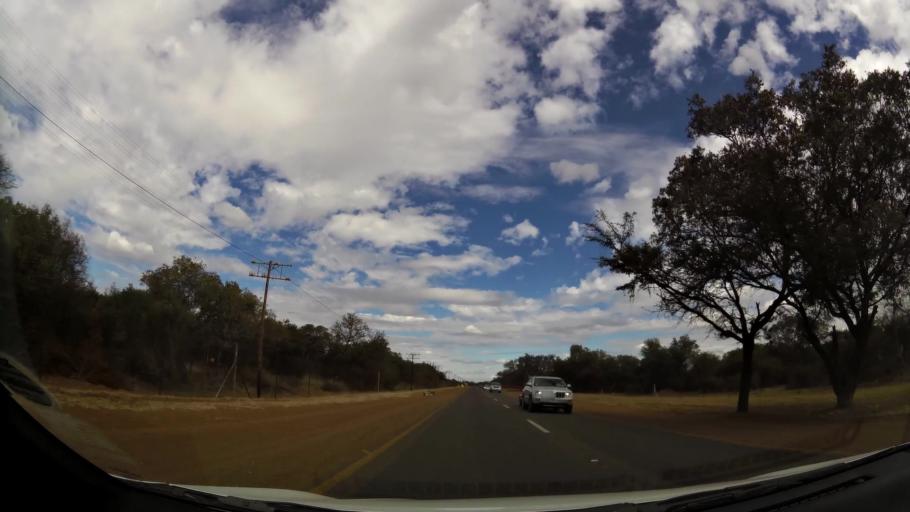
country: ZA
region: Limpopo
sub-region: Waterberg District Municipality
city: Warmbaths
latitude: -24.8952
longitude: 28.2818
